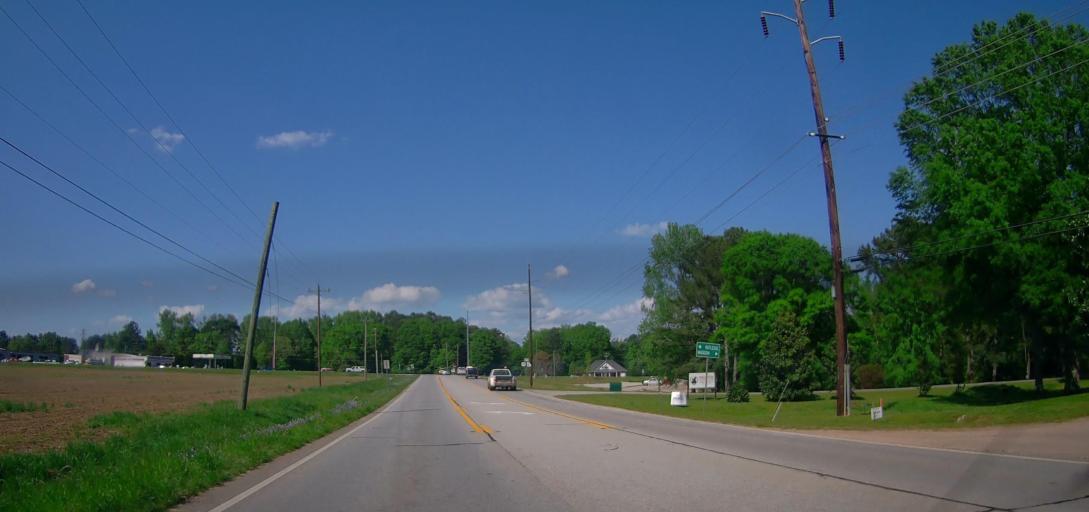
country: US
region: Georgia
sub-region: Morgan County
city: Madison
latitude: 33.5797
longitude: -83.4903
